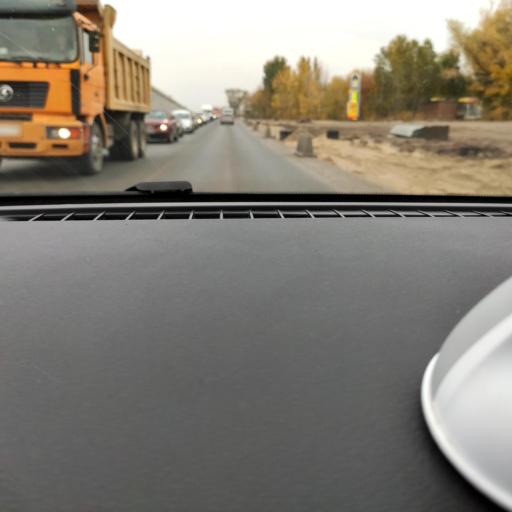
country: RU
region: Samara
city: Samara
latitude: 53.1370
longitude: 50.1036
